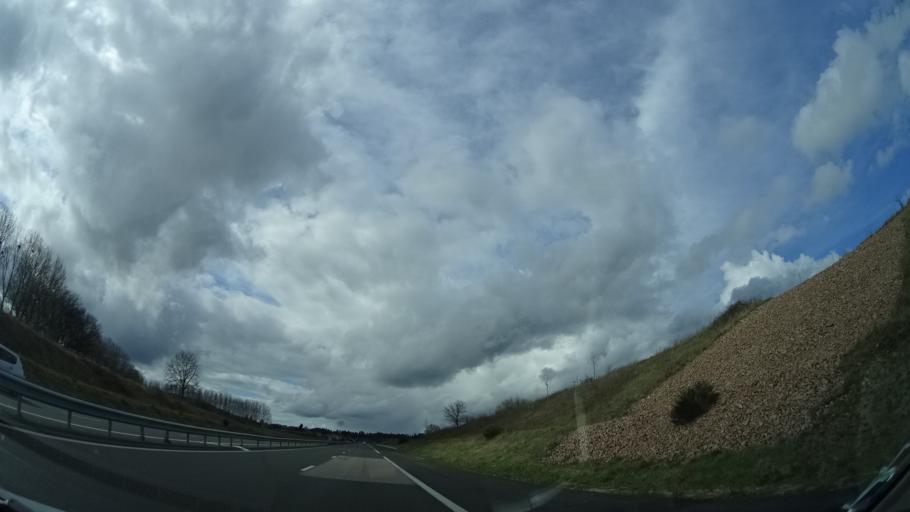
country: FR
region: Rhone-Alpes
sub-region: Departement de la Loire
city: La Pacaudiere
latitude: 46.1850
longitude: 3.8706
